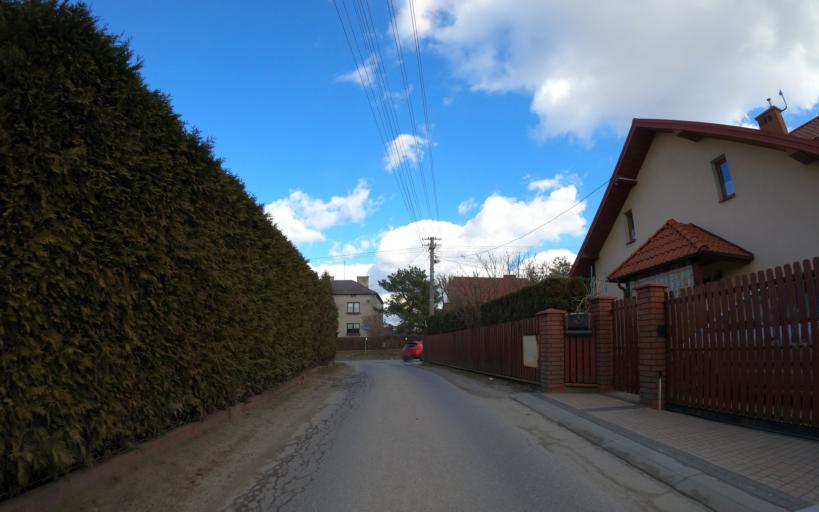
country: PL
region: Subcarpathian Voivodeship
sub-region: Powiat debicki
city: Debica
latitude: 50.0385
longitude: 21.4356
